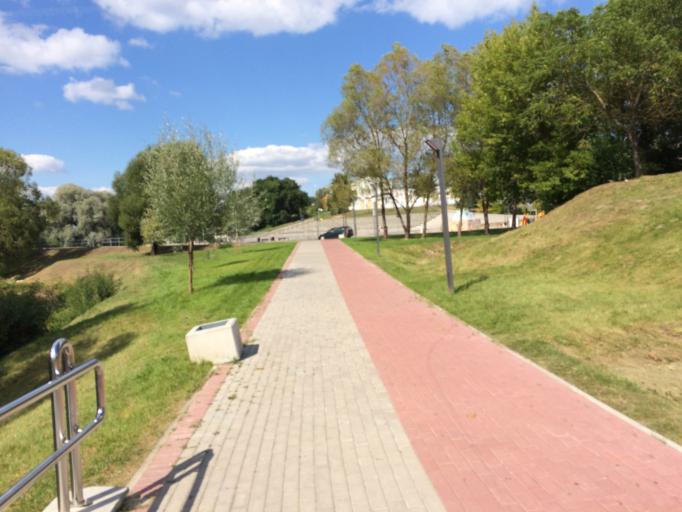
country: LV
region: Rezekne
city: Rezekne
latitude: 56.5031
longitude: 27.3276
